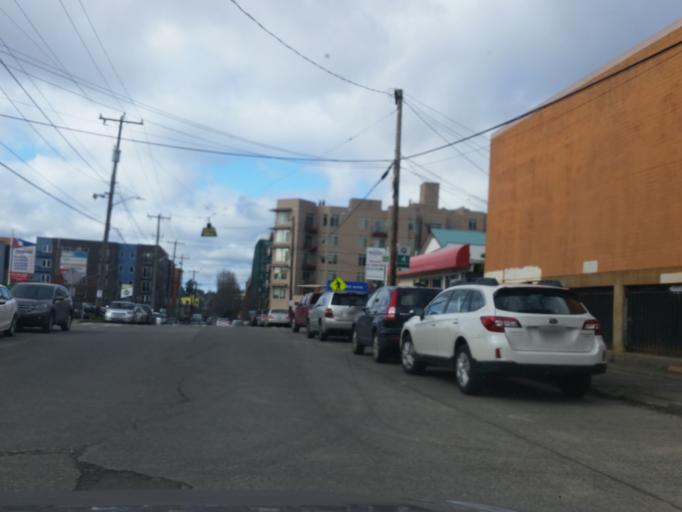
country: US
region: Washington
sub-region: King County
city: Seattle
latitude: 47.6695
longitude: -122.3855
